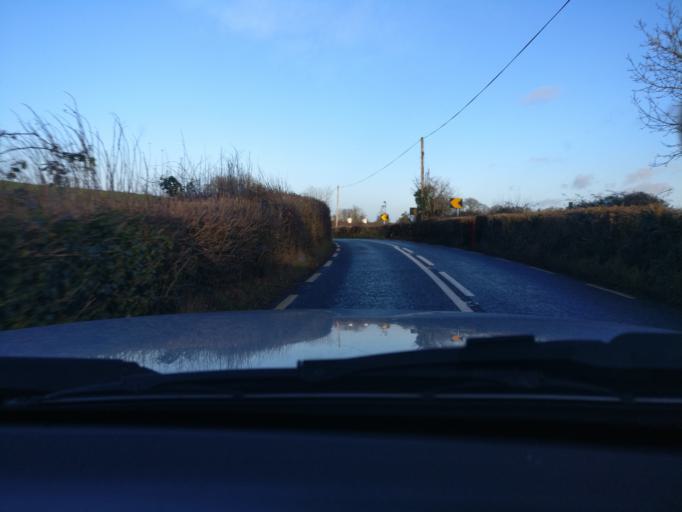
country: IE
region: Ulster
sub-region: An Cabhan
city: Kingscourt
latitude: 53.7943
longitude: -6.7182
